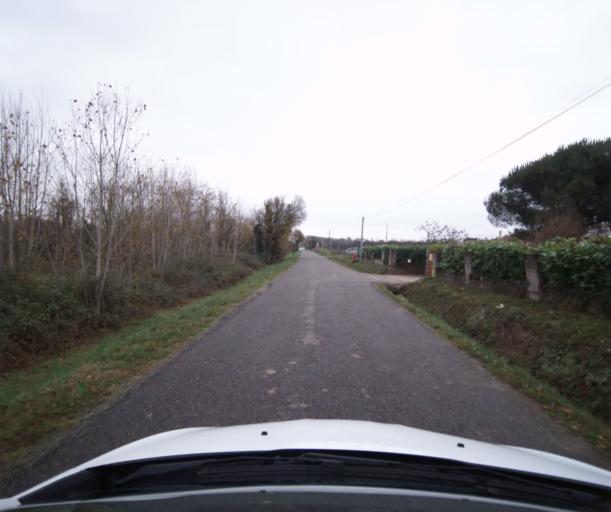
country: FR
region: Midi-Pyrenees
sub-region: Departement du Tarn-et-Garonne
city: Moissac
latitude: 44.0740
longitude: 1.1114
